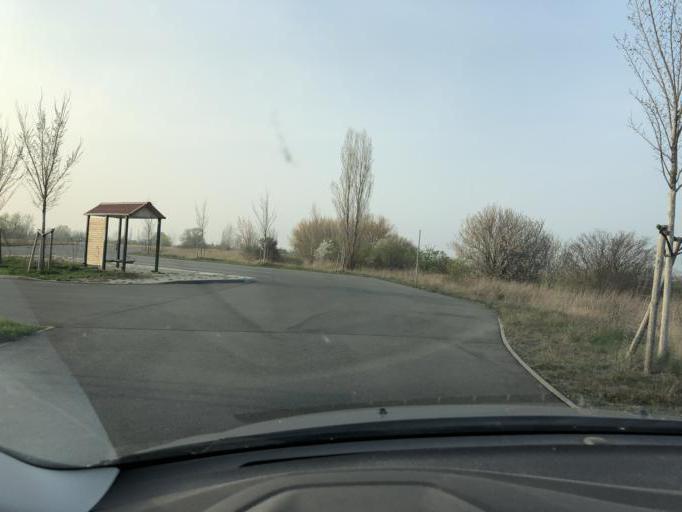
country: DE
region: Saxony
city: Dobernitz
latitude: 51.4947
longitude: 12.3233
